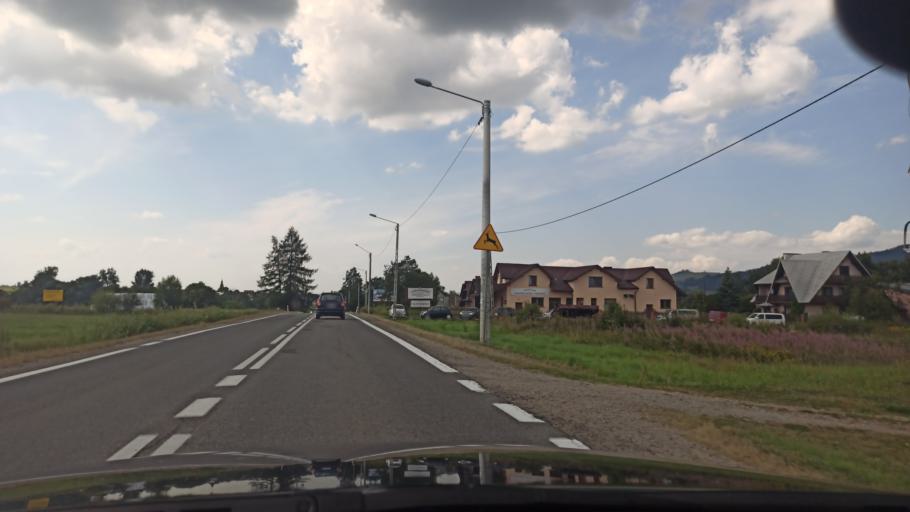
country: PL
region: Lesser Poland Voivodeship
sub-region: Powiat nowotarski
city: Lopuszna
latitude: 49.4725
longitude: 20.1170
